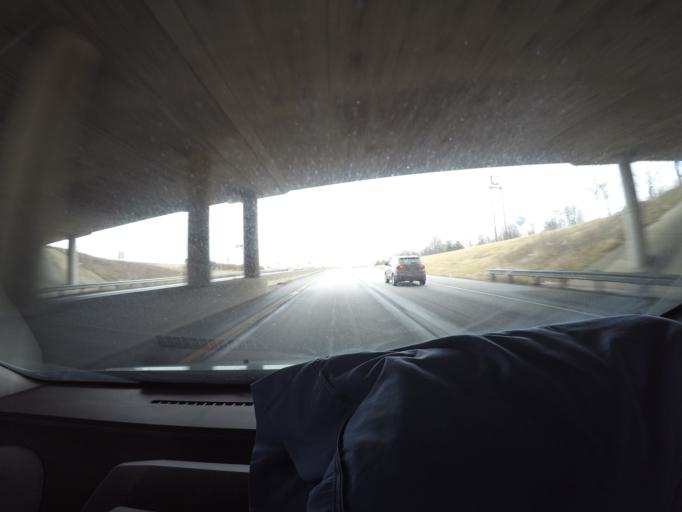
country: US
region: Missouri
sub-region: Warren County
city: Warrenton
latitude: 38.8211
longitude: -91.1391
